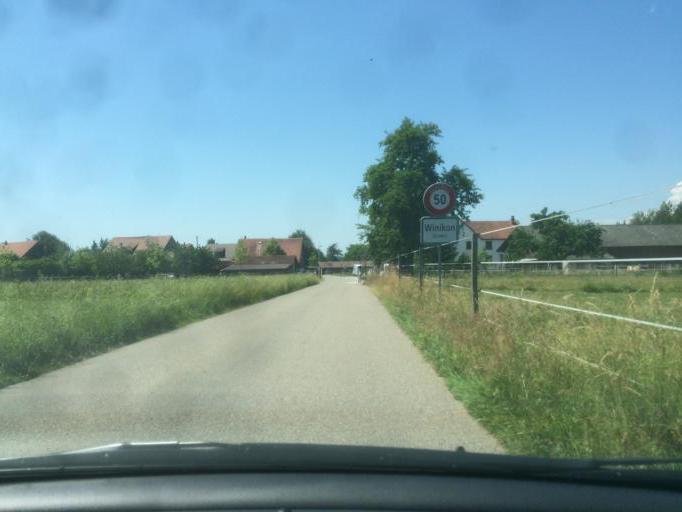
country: CH
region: Zurich
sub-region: Bezirk Uster
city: Uster / Gschwader
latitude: 47.3620
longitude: 8.7239
